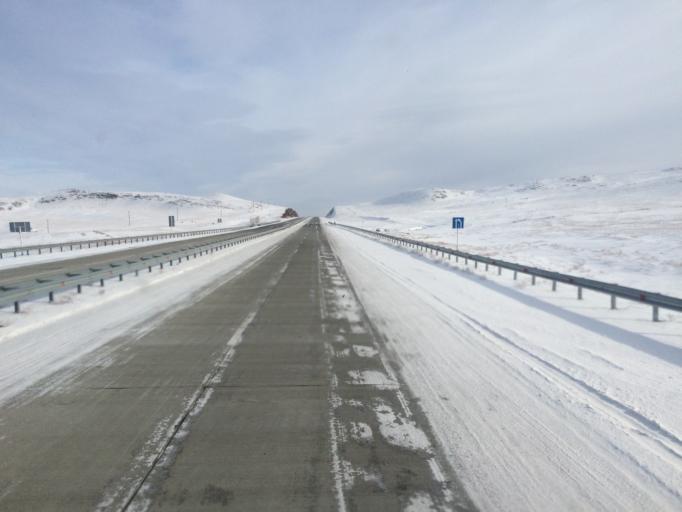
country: KZ
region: Zhambyl
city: Georgiyevka
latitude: 43.4325
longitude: 74.9367
